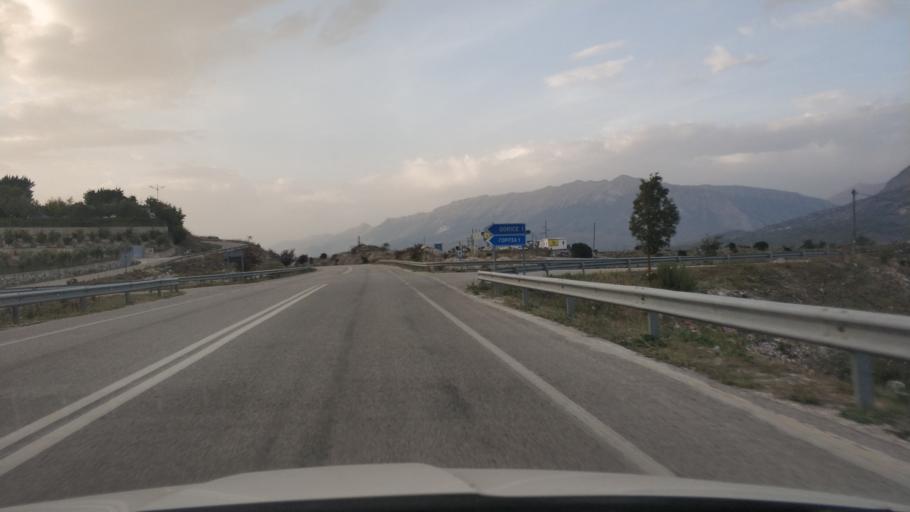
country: AL
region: Gjirokaster
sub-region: Rrethi i Gjirokastres
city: Libohove
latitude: 39.9729
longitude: 20.2360
